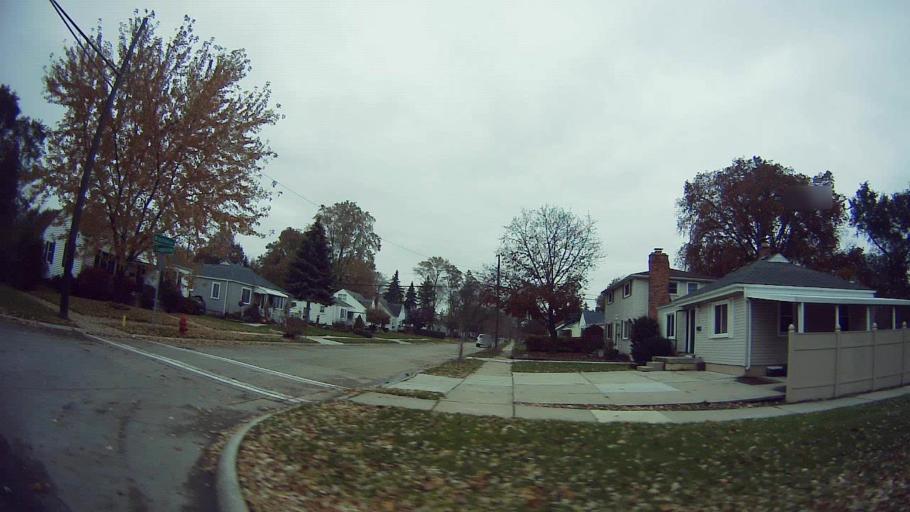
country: US
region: Michigan
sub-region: Oakland County
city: Madison Heights
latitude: 42.4800
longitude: -83.1238
